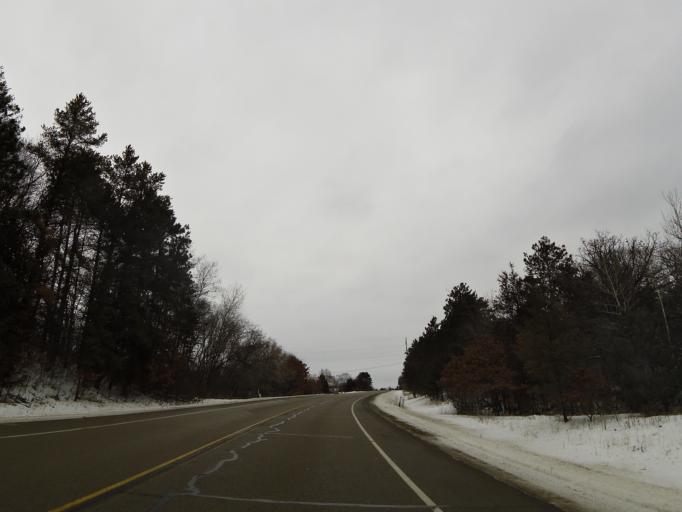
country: US
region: Minnesota
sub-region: Washington County
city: Bayport
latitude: 45.0337
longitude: -92.7537
